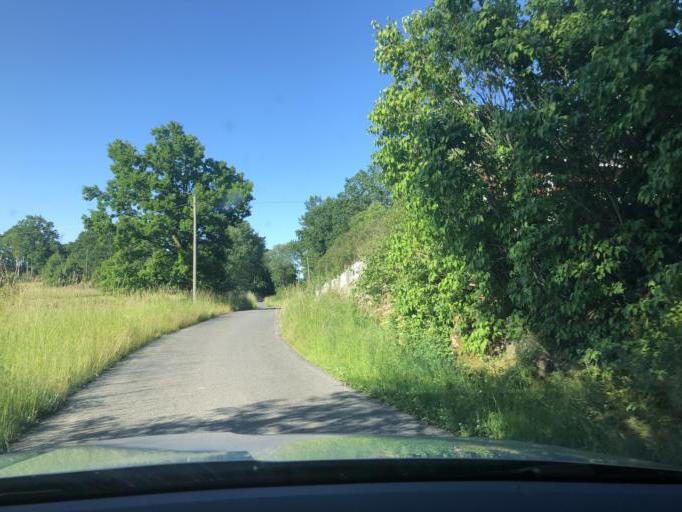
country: SE
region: Blekinge
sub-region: Karlshamns Kommun
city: Karlshamn
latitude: 56.1673
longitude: 14.8071
